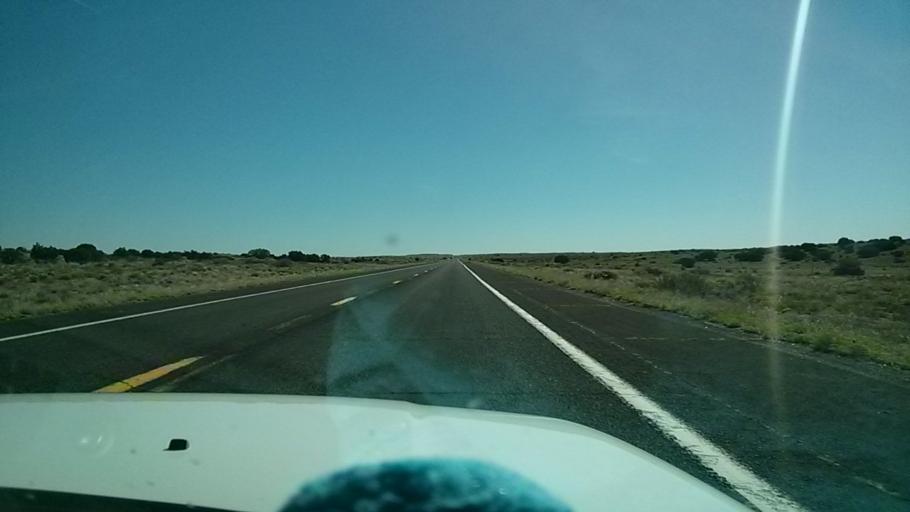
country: US
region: Arizona
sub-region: Mohave County
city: Peach Springs
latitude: 35.5052
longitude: -113.5213
